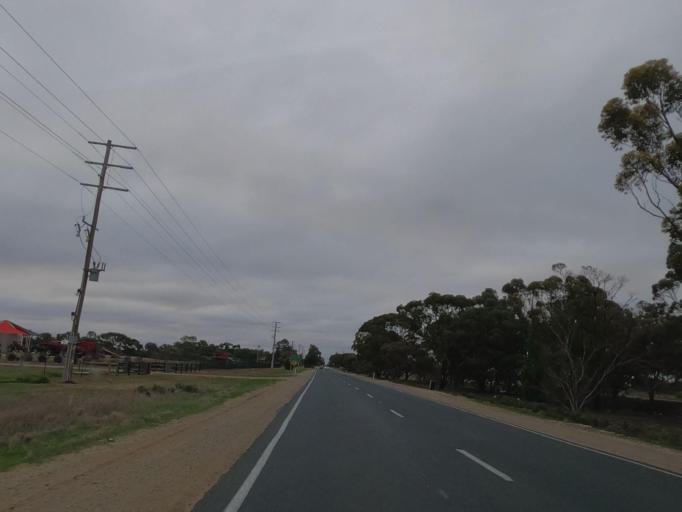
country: AU
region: Victoria
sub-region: Swan Hill
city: Swan Hill
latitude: -35.3885
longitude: 143.5687
